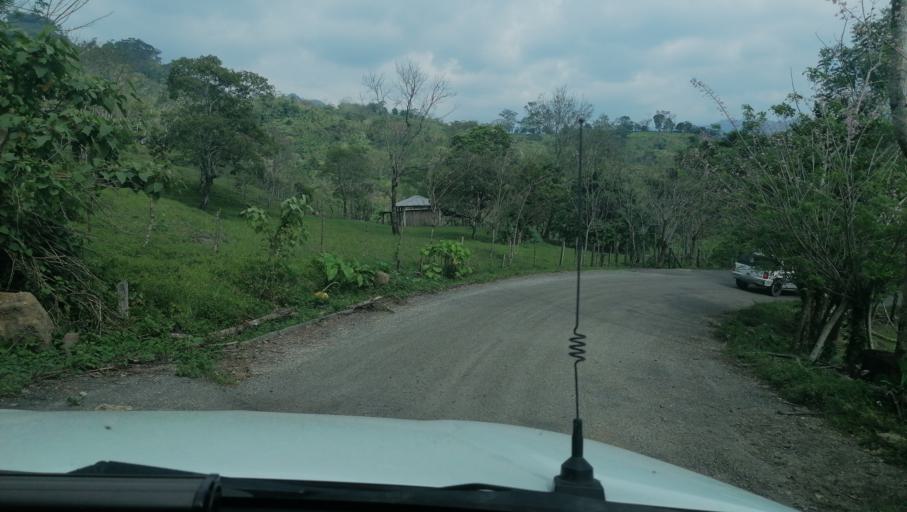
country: MX
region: Chiapas
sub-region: Francisco Leon
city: San Miguel la Sardina
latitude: 17.2292
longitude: -93.3421
